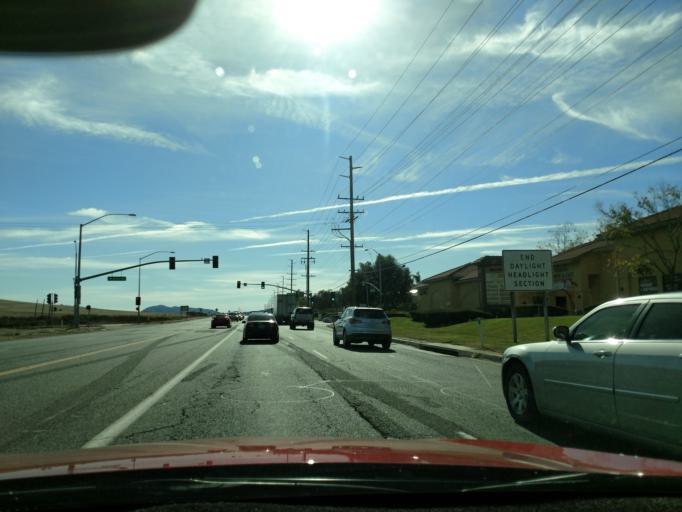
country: US
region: California
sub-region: Riverside County
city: Murrieta Hot Springs
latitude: 33.5696
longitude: -117.1365
